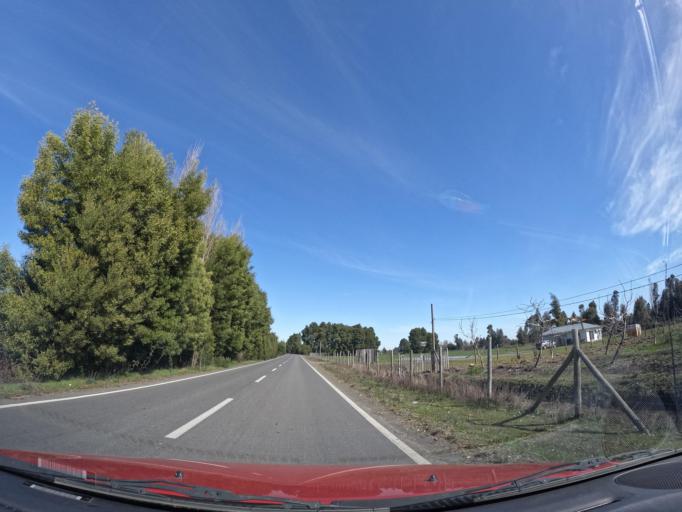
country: CL
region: Biobio
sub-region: Provincia de Biobio
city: Cabrero
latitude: -37.0348
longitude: -72.3717
